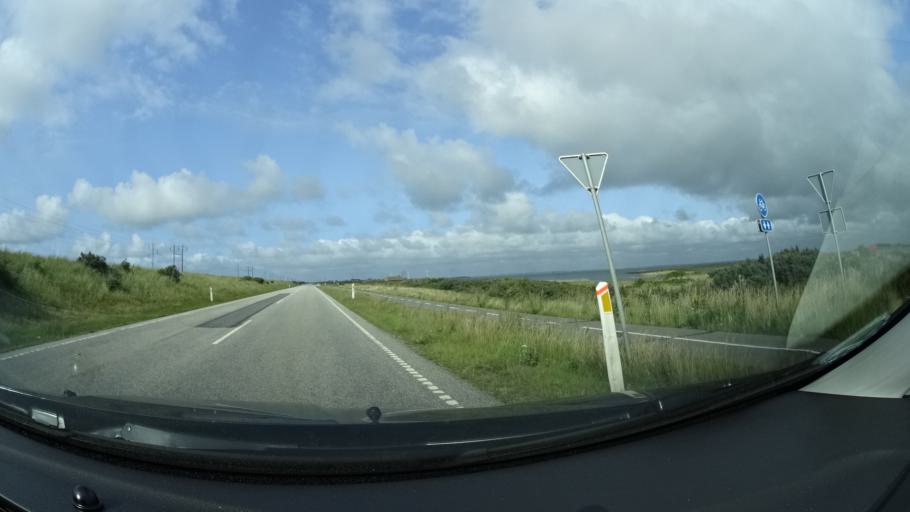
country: DK
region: Central Jutland
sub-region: Lemvig Kommune
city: Harboore
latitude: 56.6318
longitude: 8.1844
